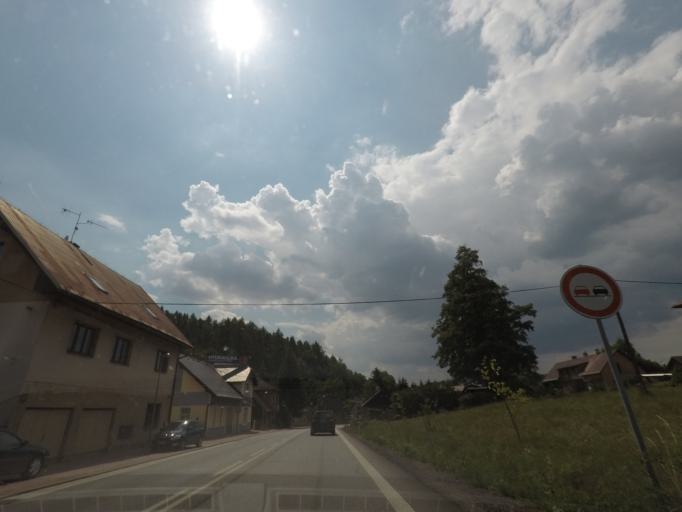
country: CZ
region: Kralovehradecky
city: Nova Paka
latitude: 50.4991
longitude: 15.5272
